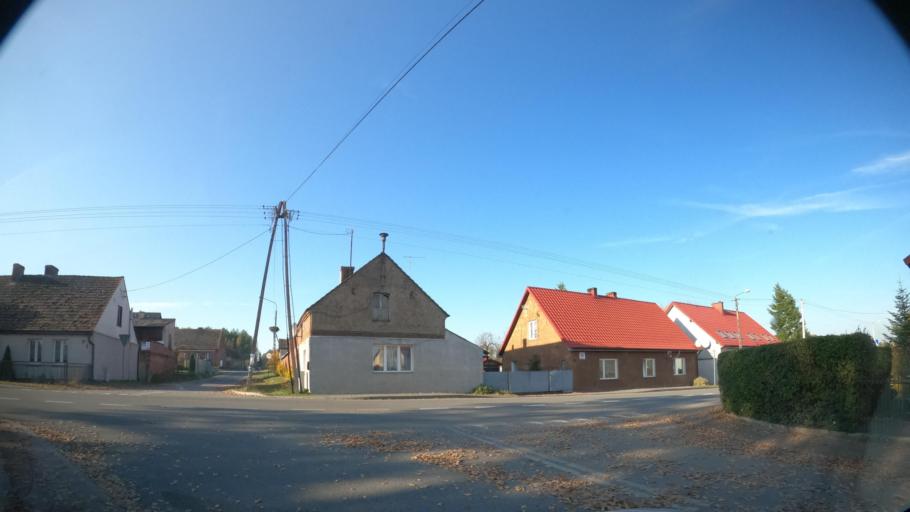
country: PL
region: West Pomeranian Voivodeship
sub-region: Powiat walecki
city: Walcz
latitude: 53.2999
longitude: 16.5291
